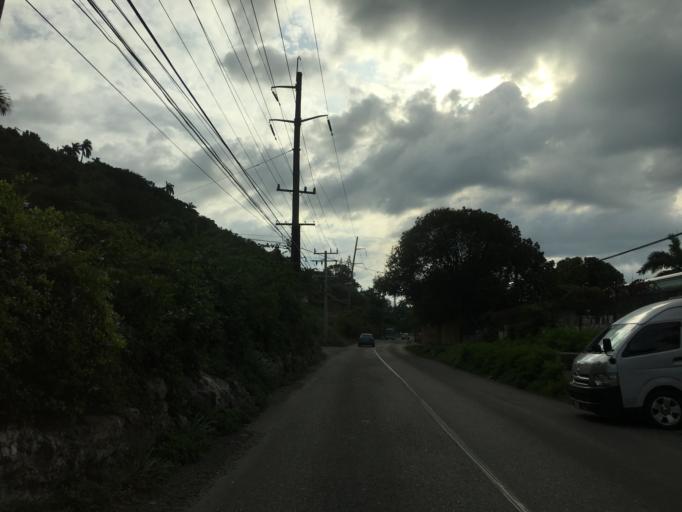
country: JM
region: Saint James
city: Montego Bay
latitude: 18.4934
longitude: -77.9183
